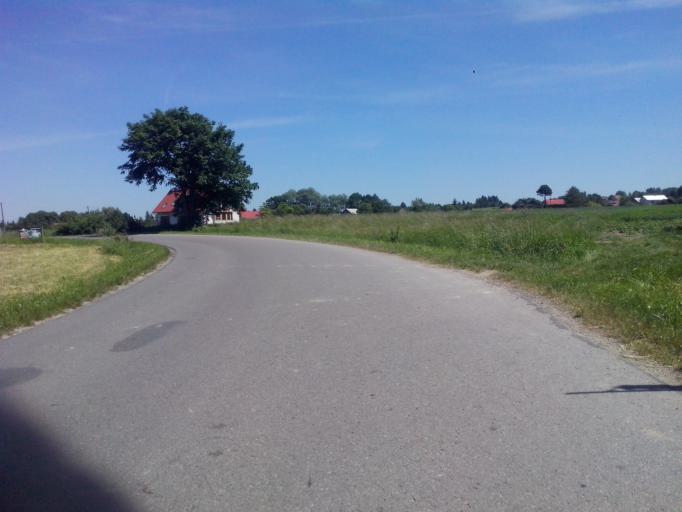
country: PL
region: Subcarpathian Voivodeship
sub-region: Powiat strzyzowski
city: Wisniowa
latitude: 49.8571
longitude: 21.6985
